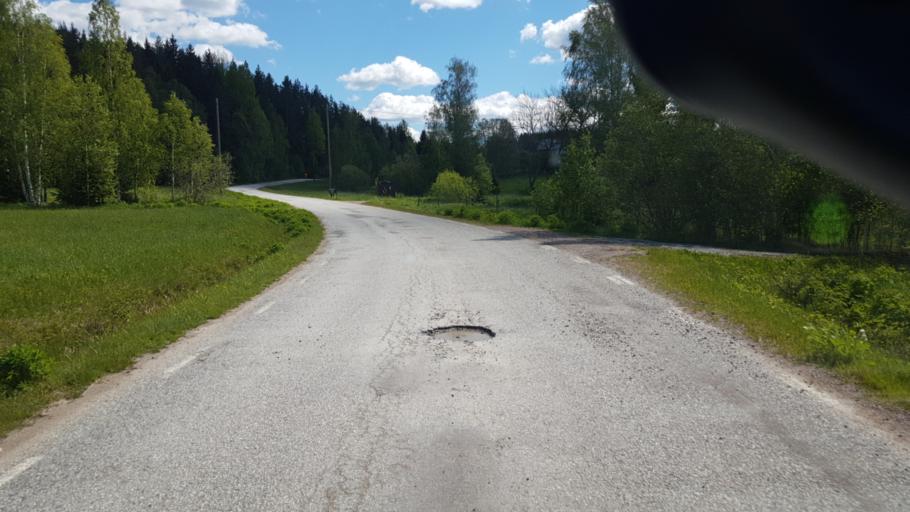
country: SE
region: Vaermland
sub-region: Sunne Kommun
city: Sunne
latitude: 59.6693
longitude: 12.9066
